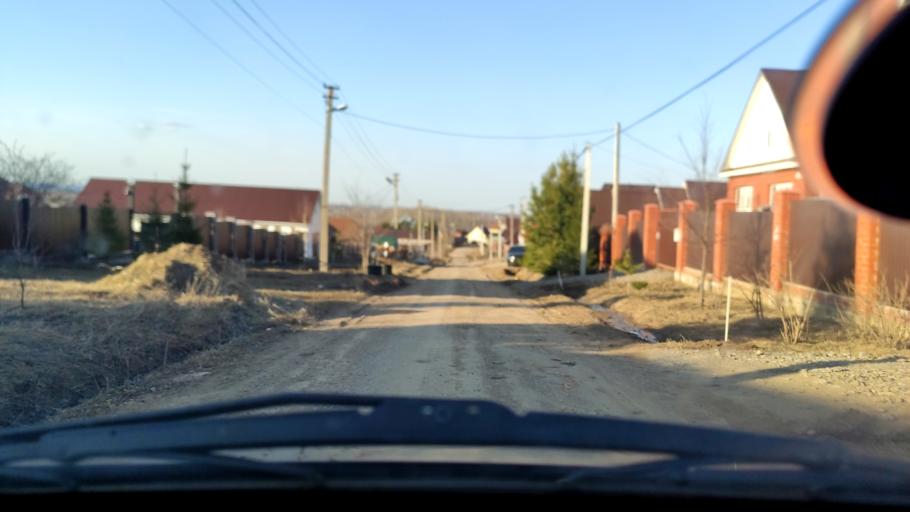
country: RU
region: Bashkortostan
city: Kabakovo
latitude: 54.6323
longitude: 56.0662
